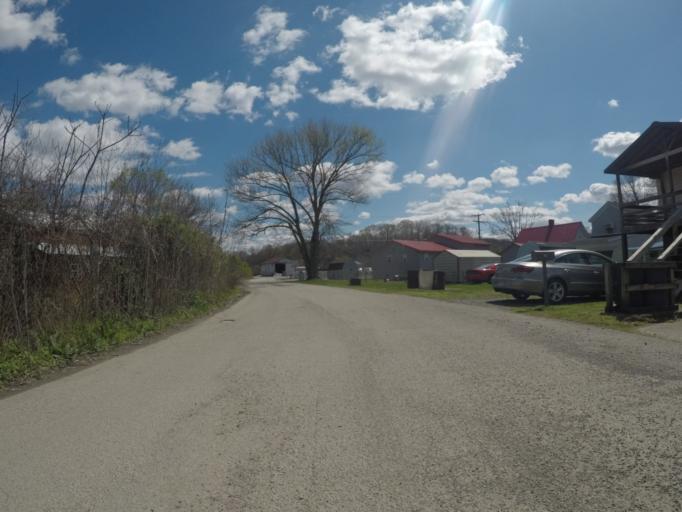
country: US
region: West Virginia
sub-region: Wayne County
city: Kenova
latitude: 38.3956
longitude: -82.5750
